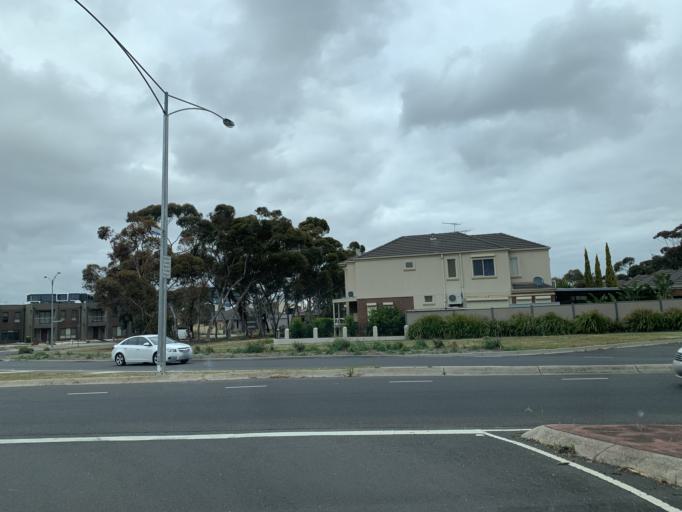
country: AU
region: Victoria
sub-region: Brimbank
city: Cairnlea
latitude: -37.7548
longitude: 144.7910
